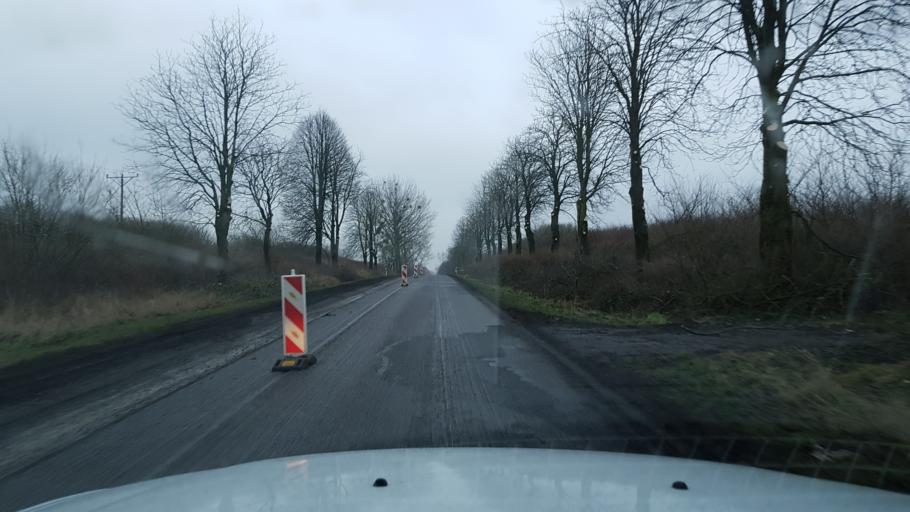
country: PL
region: West Pomeranian Voivodeship
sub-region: Powiat gryficki
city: Ploty
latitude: 53.8323
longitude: 15.2434
